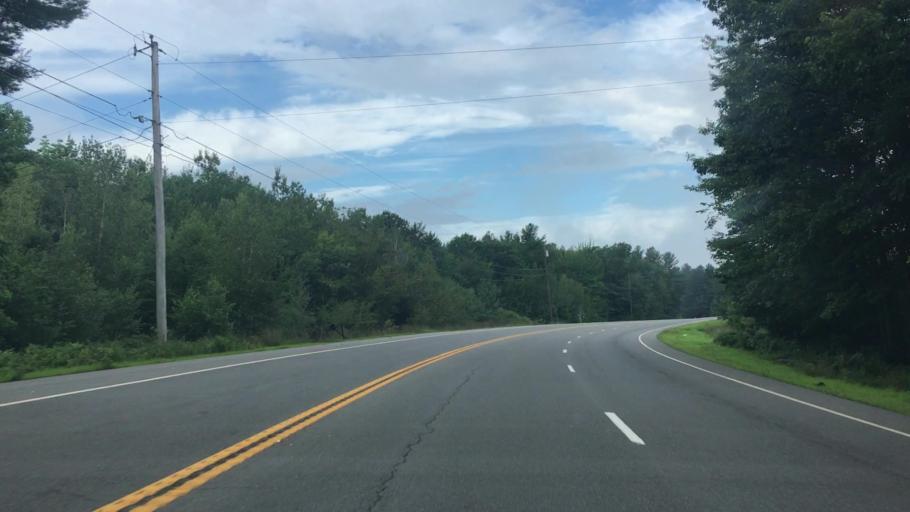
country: US
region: Maine
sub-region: York County
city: Sanford (historical)
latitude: 43.4296
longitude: -70.7981
